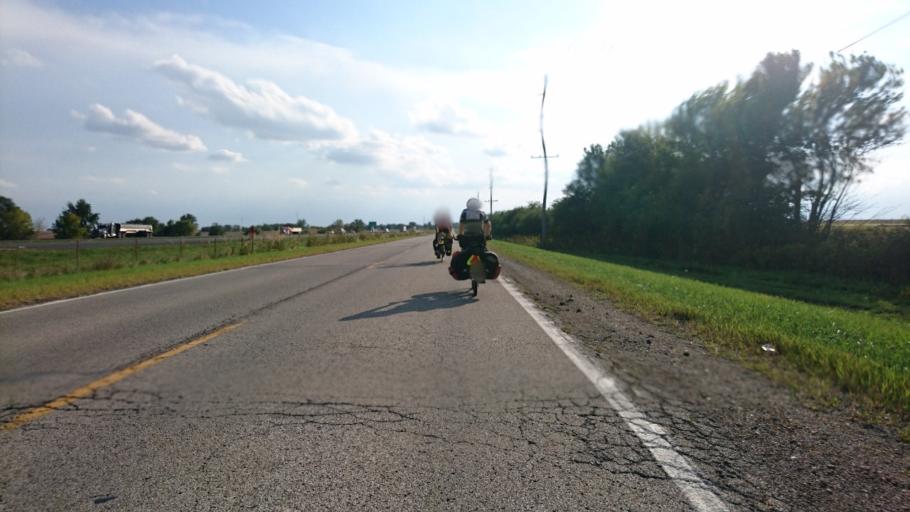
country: US
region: Illinois
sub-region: Logan County
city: Atlanta
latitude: 40.2827
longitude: -89.2065
